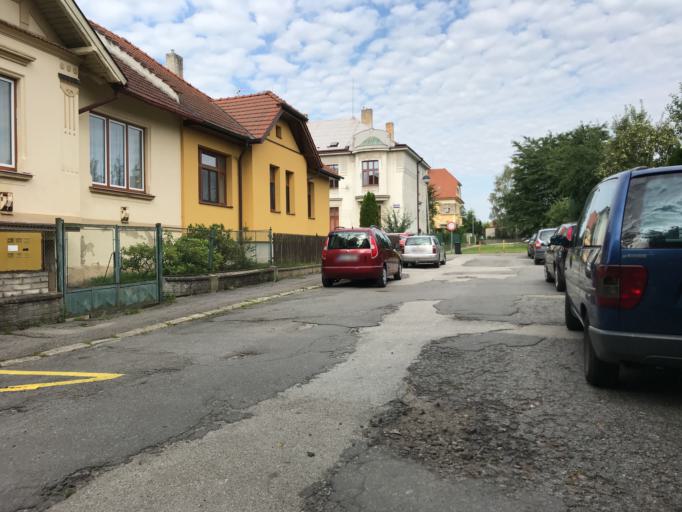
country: CZ
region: Jihocesky
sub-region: Okres Jindrichuv Hradec
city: Trebon
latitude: 49.0069
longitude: 14.7658
